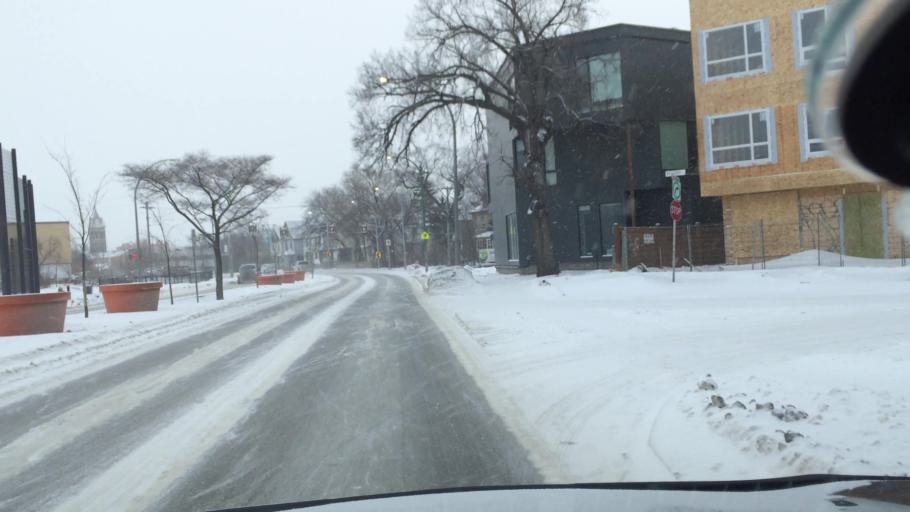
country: CA
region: Manitoba
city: Winnipeg
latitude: 49.8864
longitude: -97.1641
